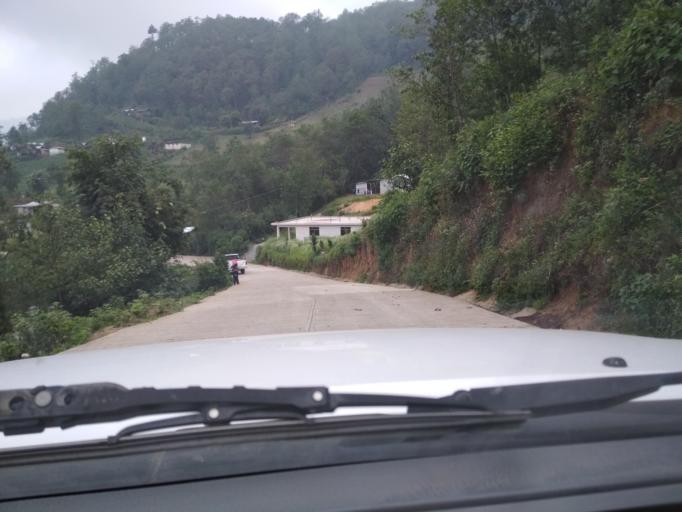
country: MX
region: Veracruz
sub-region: La Perla
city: Chilapa
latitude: 18.9888
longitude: -97.1551
